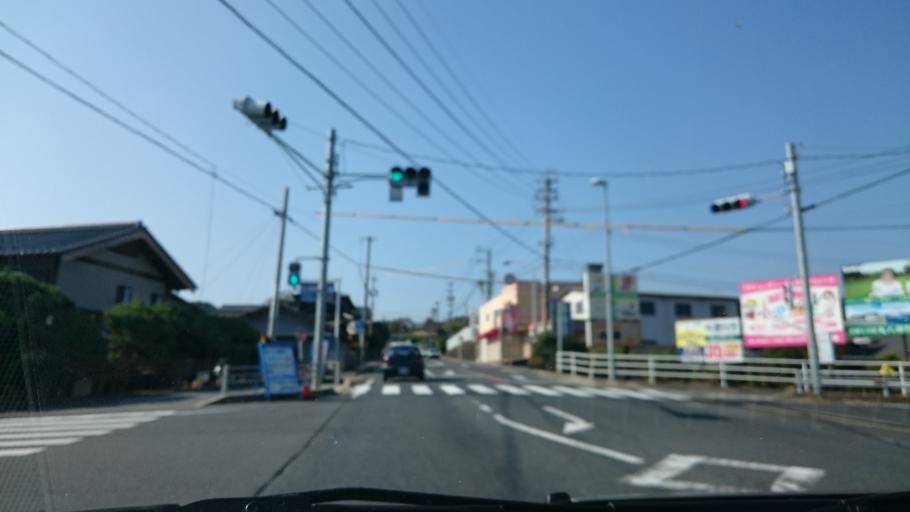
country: JP
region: Gifu
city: Nakatsugawa
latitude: 35.4926
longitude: 137.4873
